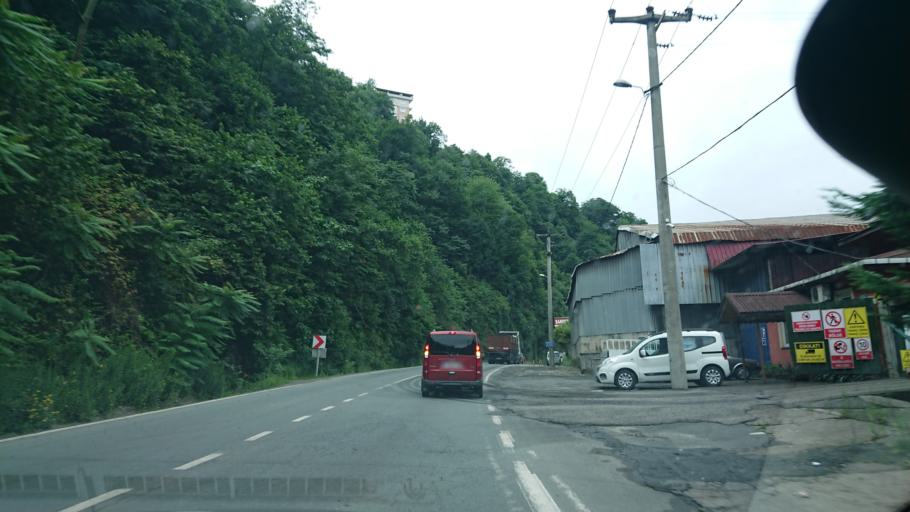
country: TR
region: Rize
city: Gundogdu
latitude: 41.0348
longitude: 40.5796
